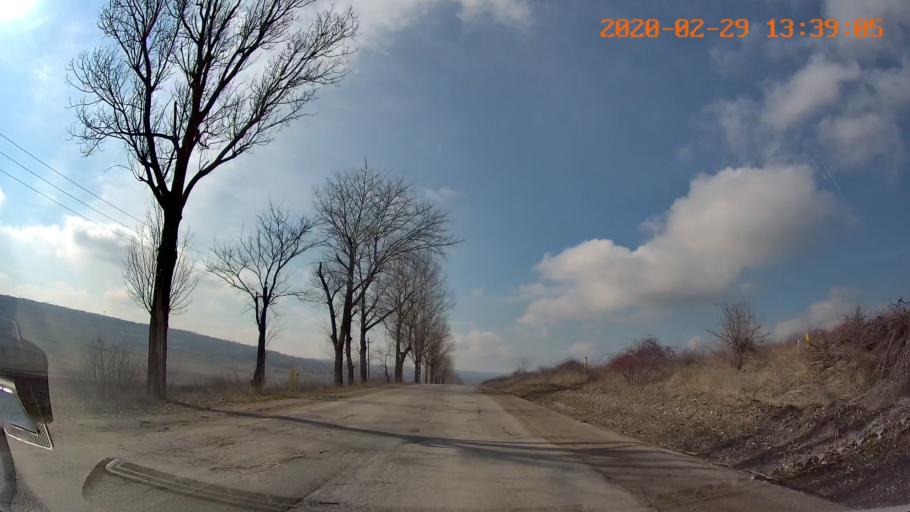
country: MD
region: Floresti
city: Leninskiy
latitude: 47.8514
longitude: 28.5871
